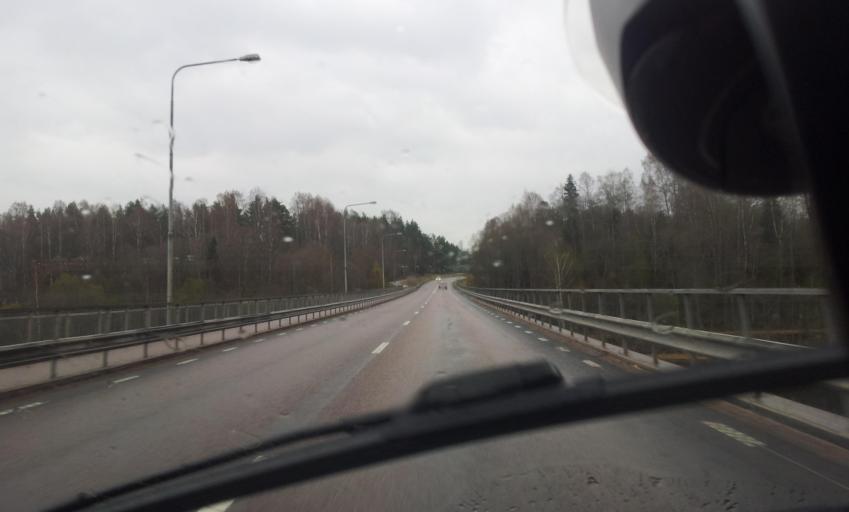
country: SE
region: Dalarna
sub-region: Borlange Kommun
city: Borlaenge
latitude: 60.5145
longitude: 15.3761
